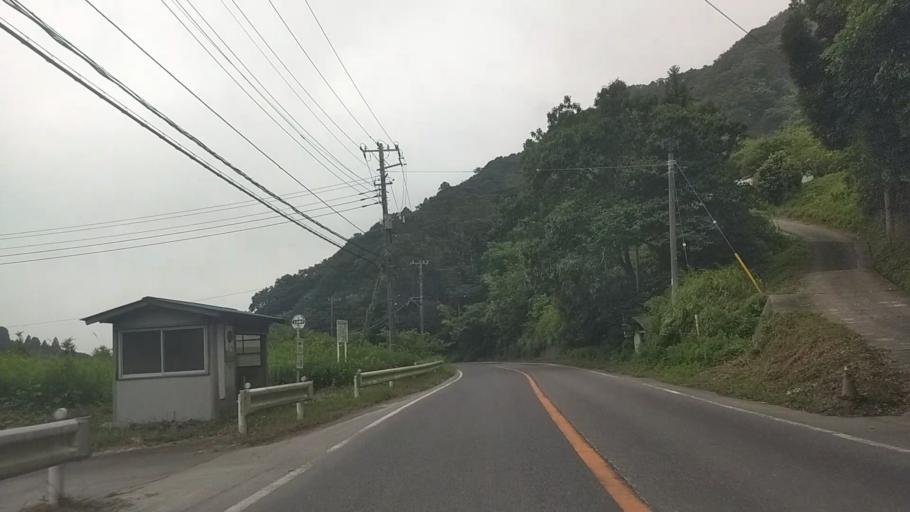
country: JP
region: Chiba
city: Tateyama
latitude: 35.1444
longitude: 139.8675
